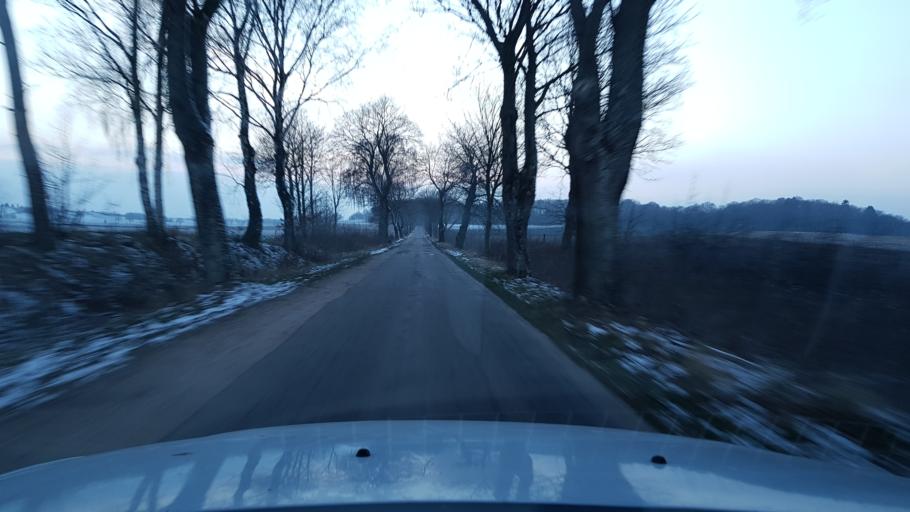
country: PL
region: West Pomeranian Voivodeship
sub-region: Powiat swidwinski
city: Slawoborze
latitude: 53.9739
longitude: 15.7770
